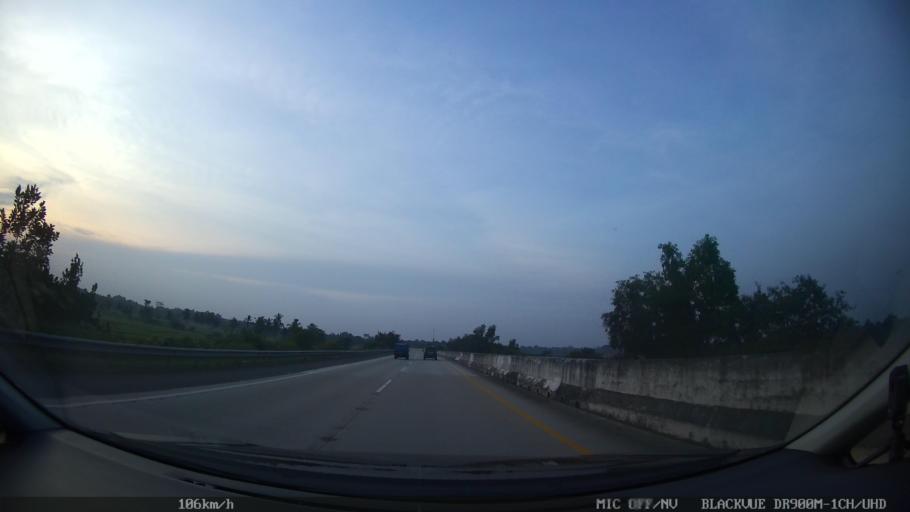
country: ID
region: Lampung
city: Penengahan
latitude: -5.7573
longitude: 105.7109
